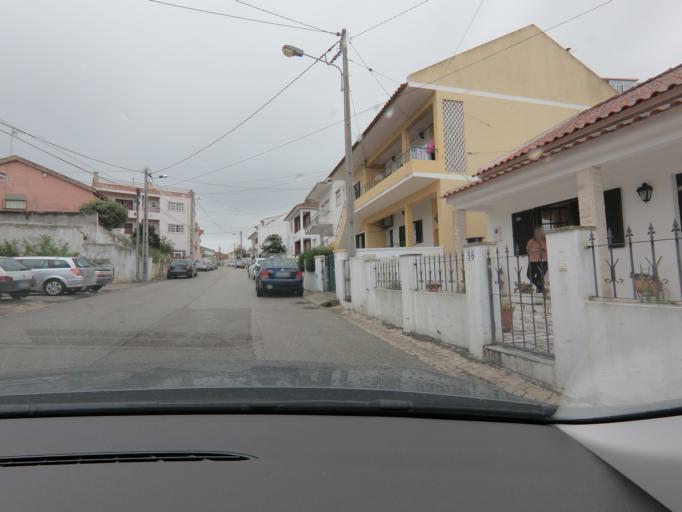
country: PT
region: Lisbon
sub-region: Alenquer
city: Alenquer
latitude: 39.0471
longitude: -9.0028
